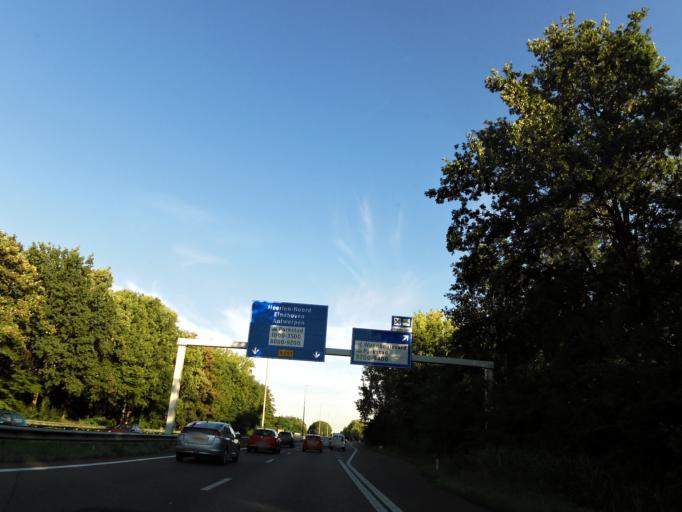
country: NL
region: Limburg
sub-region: Gemeente Heerlen
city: Heerlen
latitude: 50.8880
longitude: 5.9640
